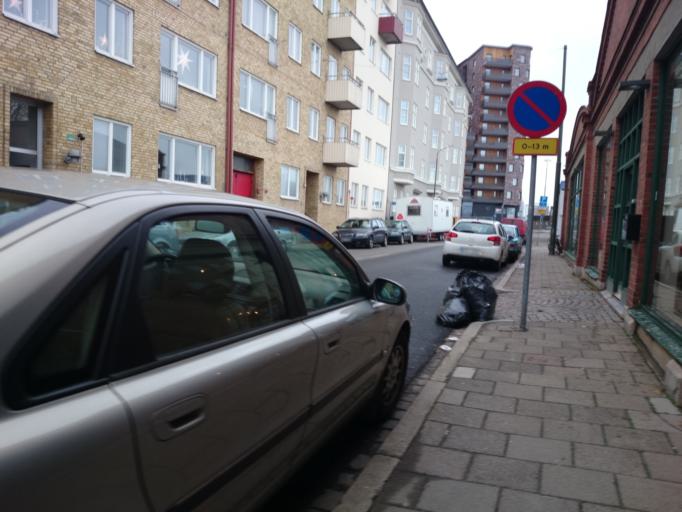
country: SE
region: Skane
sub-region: Malmo
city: Malmoe
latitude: 55.6088
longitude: 13.0155
